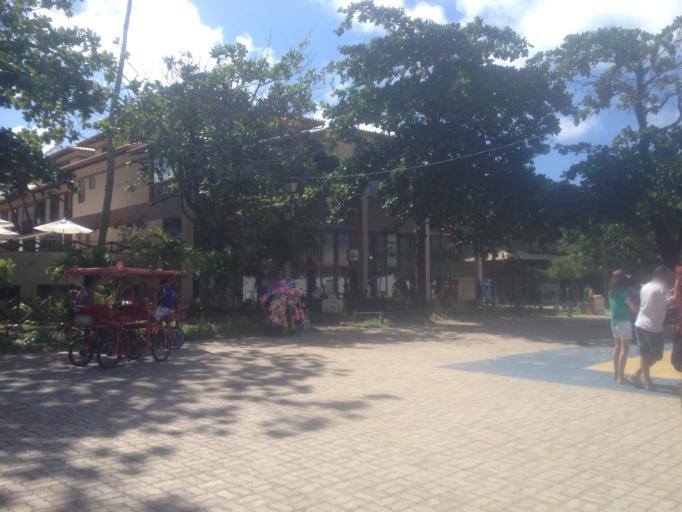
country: BR
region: Bahia
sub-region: Mata De Sao Joao
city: Mata de Sao Joao
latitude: -12.5777
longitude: -38.0032
